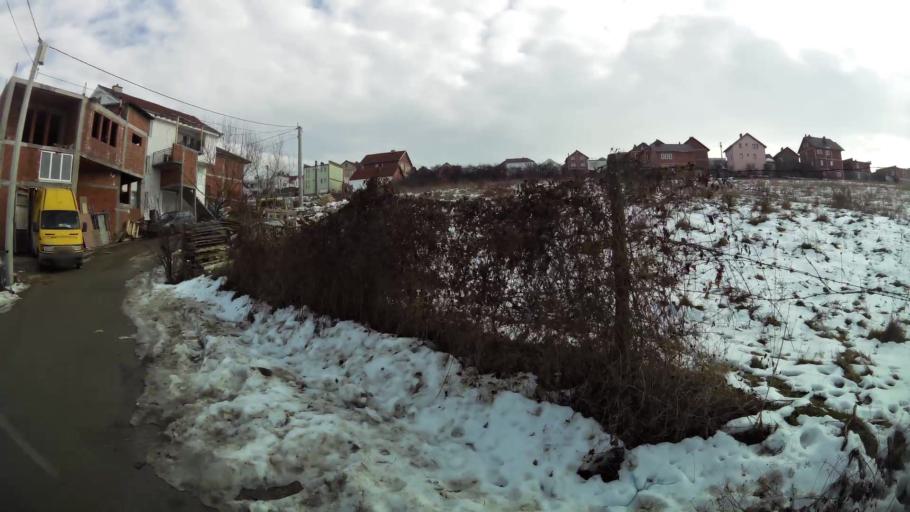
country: XK
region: Pristina
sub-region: Komuna e Prishtines
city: Pristina
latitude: 42.6777
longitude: 21.1527
